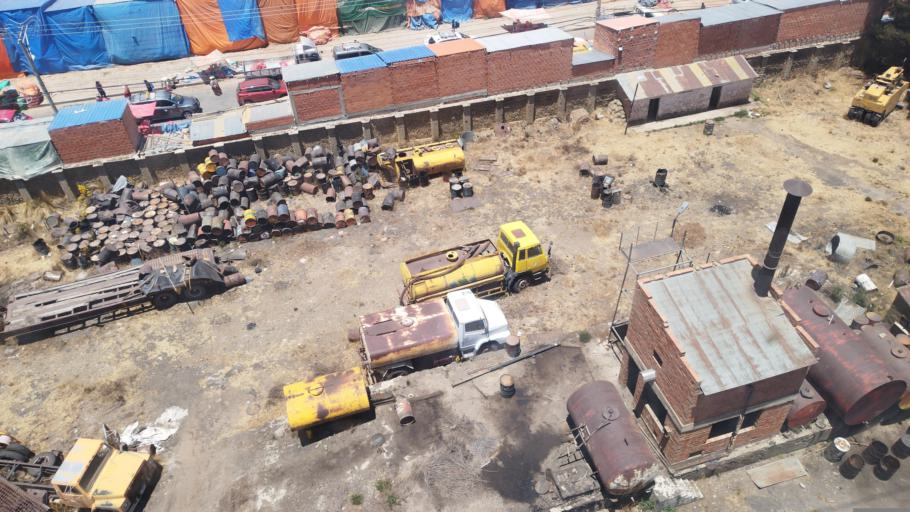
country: BO
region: La Paz
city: La Paz
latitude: -16.5079
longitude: -68.1572
